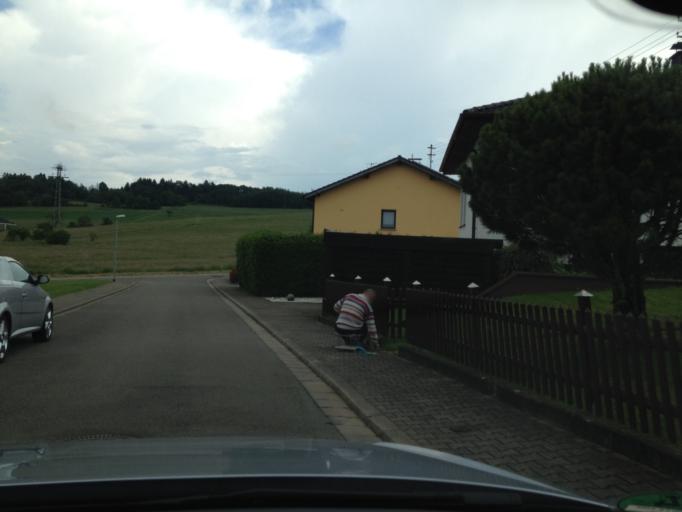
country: DE
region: Rheinland-Pfalz
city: Reichweiler
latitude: 49.5312
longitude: 7.2805
